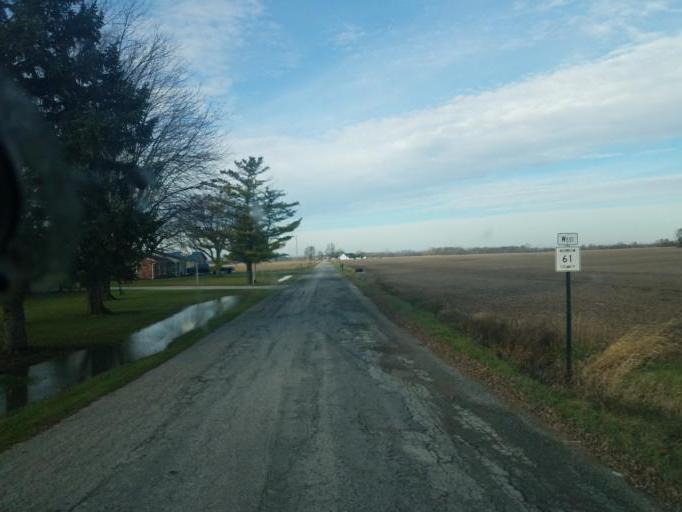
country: US
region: Ohio
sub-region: Morrow County
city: Mount Gilead
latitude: 40.6162
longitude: -82.9186
